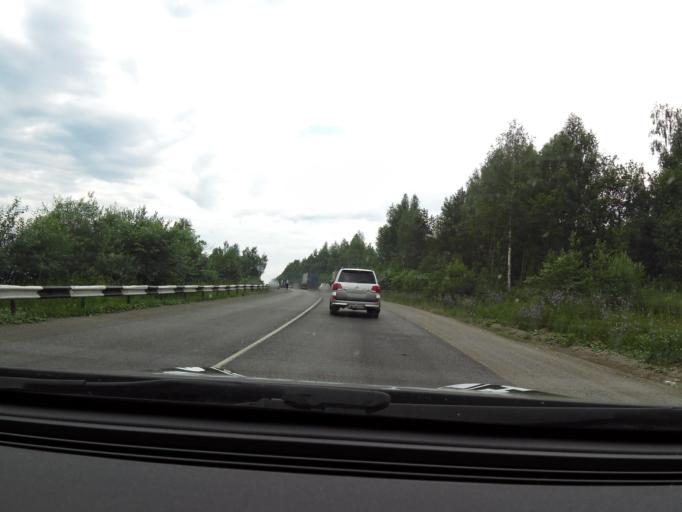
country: RU
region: Chelyabinsk
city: Sim
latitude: 54.9996
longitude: 57.6169
